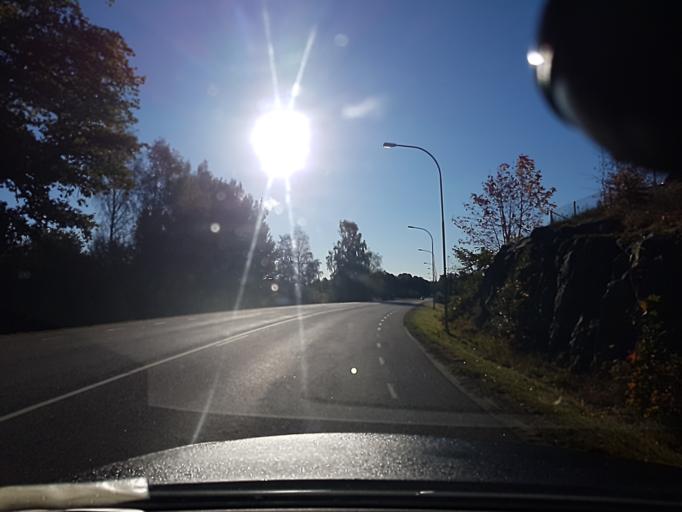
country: SE
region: Kronoberg
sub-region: Vaxjo Kommun
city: Vaexjoe
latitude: 56.8699
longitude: 14.8279
